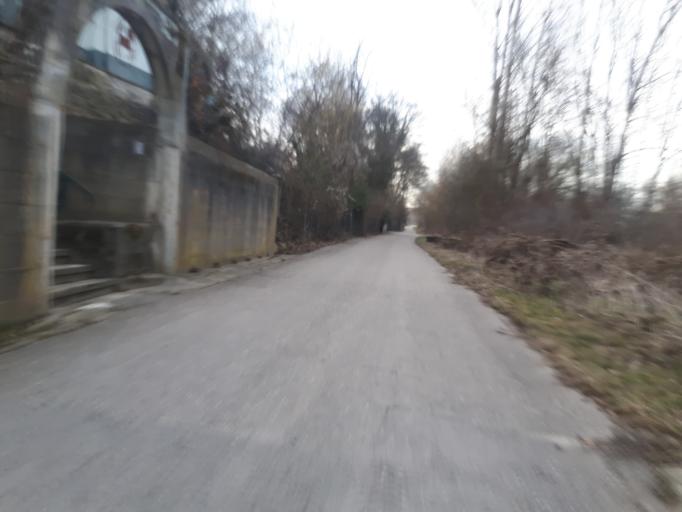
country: DE
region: Baden-Wuerttemberg
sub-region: Regierungsbezirk Stuttgart
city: Oedheim
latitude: 49.2532
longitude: 9.2890
